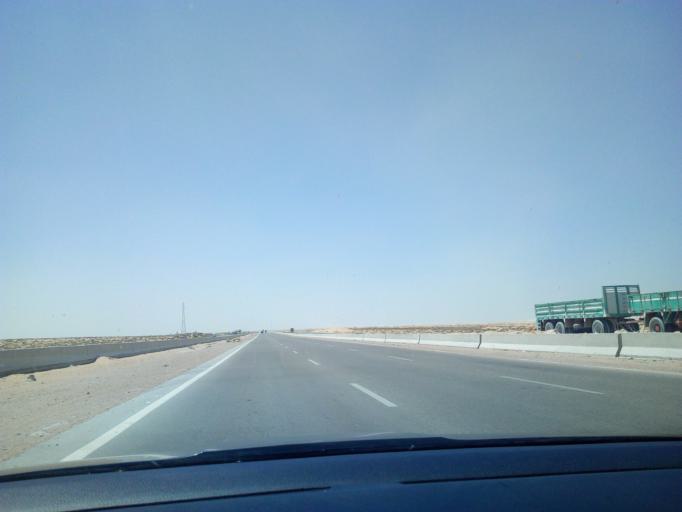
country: EG
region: Al Buhayrah
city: Abu al Matamir
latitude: 30.6218
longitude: 29.7931
